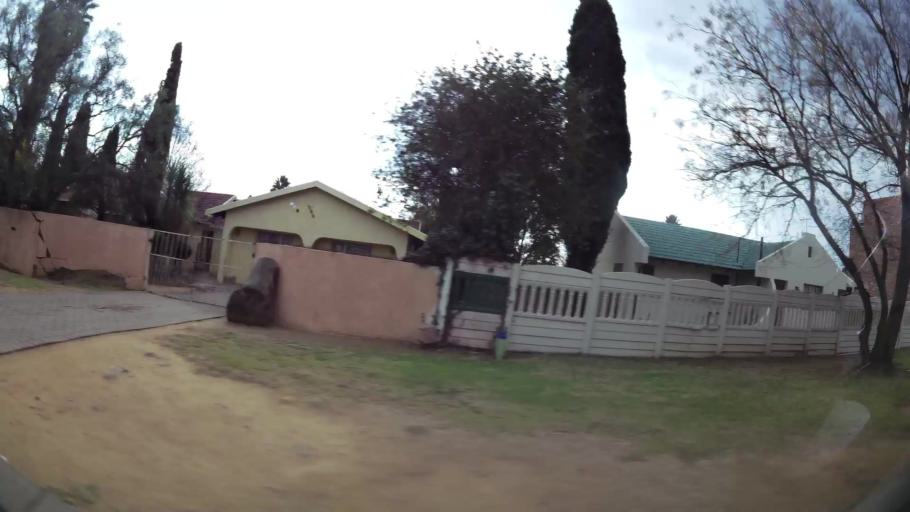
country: ZA
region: Gauteng
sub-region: Ekurhuleni Metropolitan Municipality
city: Benoni
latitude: -26.1167
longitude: 28.3714
